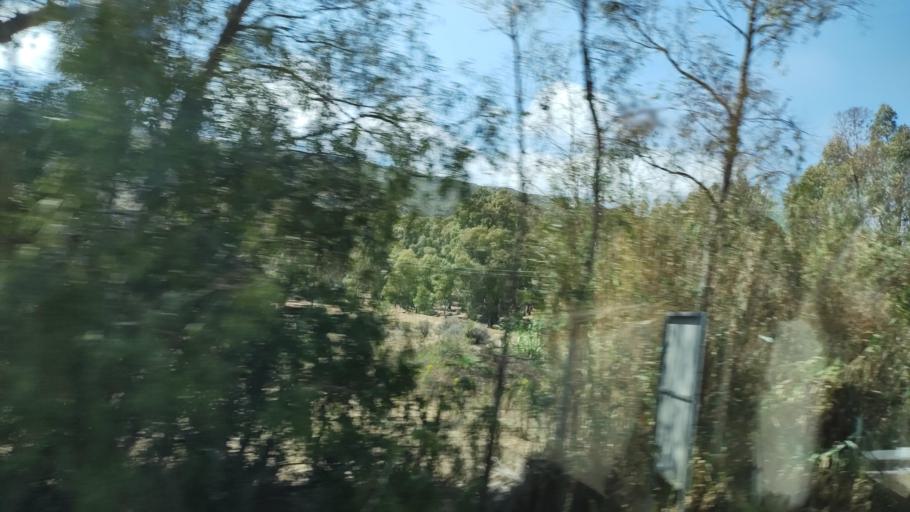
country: ES
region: Andalusia
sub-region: Provincia de Cadiz
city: La Linea de la Concepcion
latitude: 36.1958
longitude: -5.3474
